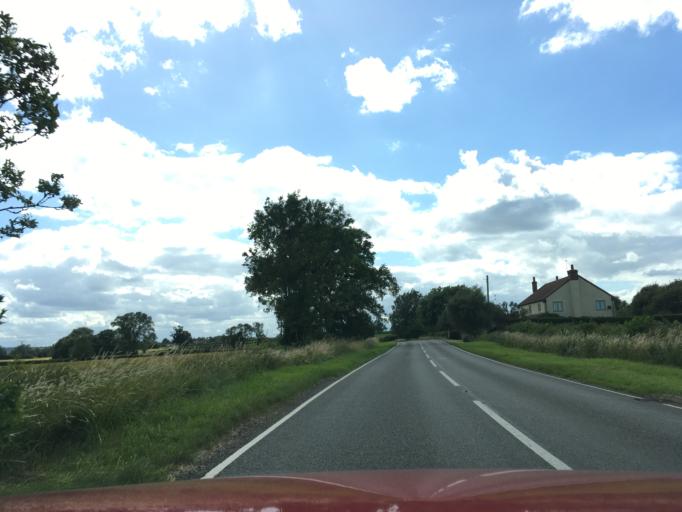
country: GB
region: England
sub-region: Leicestershire
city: Shepshed
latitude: 52.7874
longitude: -1.3155
